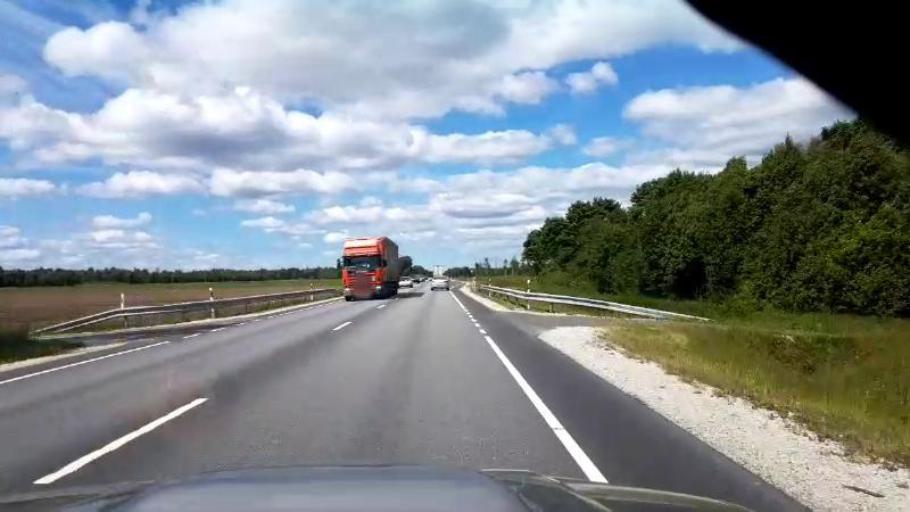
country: EE
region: Paernumaa
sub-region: Halinga vald
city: Parnu-Jaagupi
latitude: 58.6408
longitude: 24.4907
